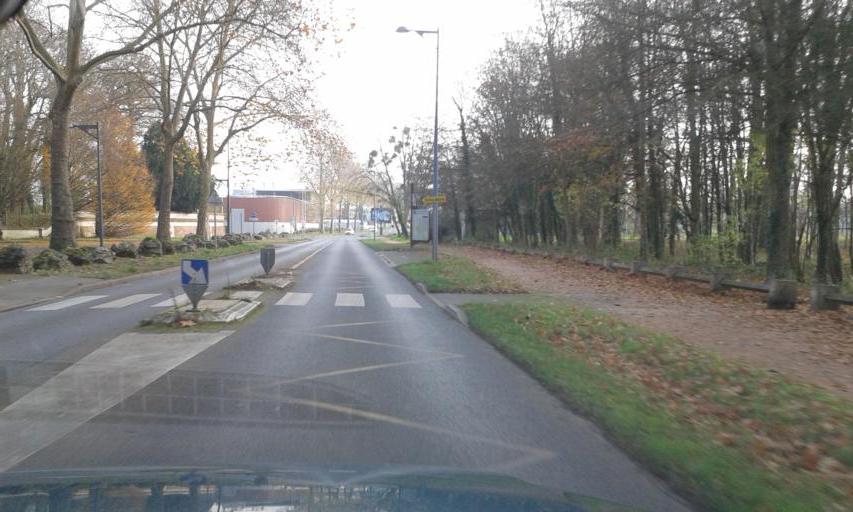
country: FR
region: Centre
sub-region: Departement du Loiret
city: Saint-Cyr-en-Val
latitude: 47.8469
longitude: 1.9390
